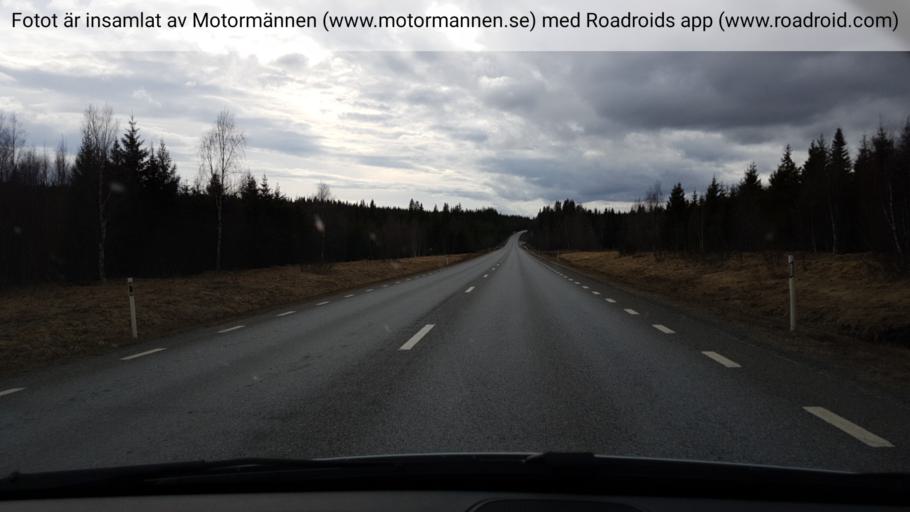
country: SE
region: Jaemtland
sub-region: Krokoms Kommun
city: Valla
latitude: 63.3121
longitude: 13.7515
